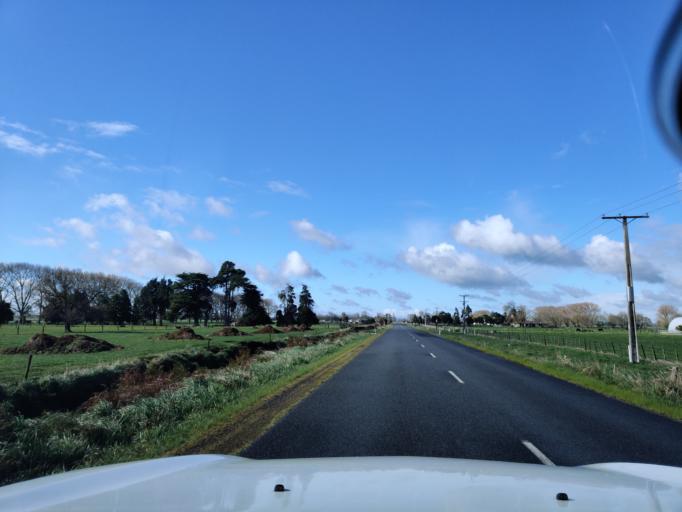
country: NZ
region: Waikato
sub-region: Waikato District
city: Ngaruawahia
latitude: -37.5900
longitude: 175.2899
